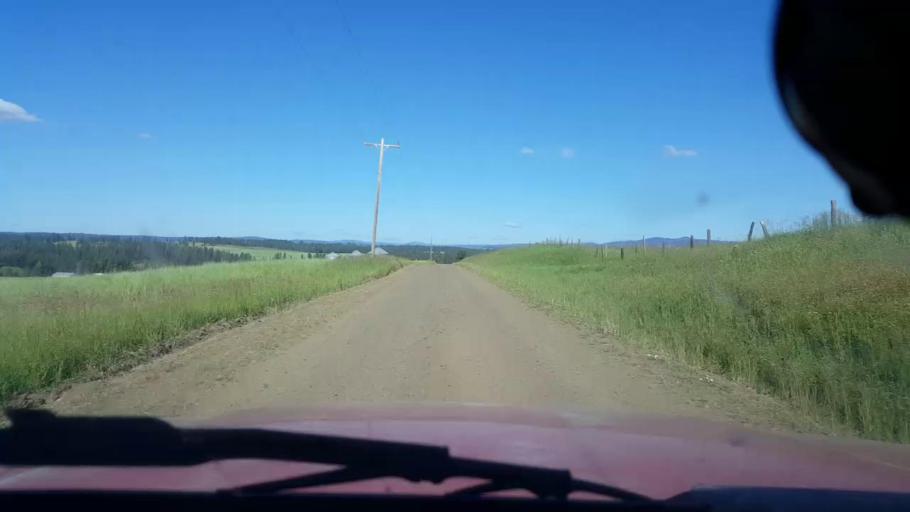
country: US
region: Washington
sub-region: Garfield County
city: Pomeroy
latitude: 45.9846
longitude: -117.4592
